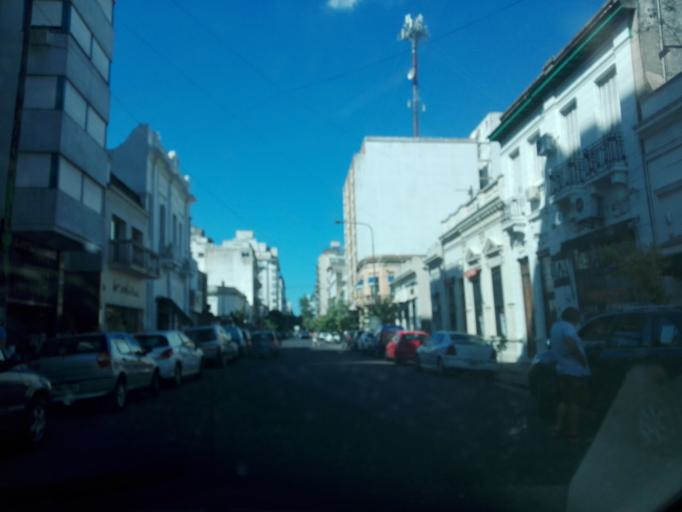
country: AR
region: Buenos Aires
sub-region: Partido de La Plata
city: La Plata
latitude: -34.9166
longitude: -57.9530
